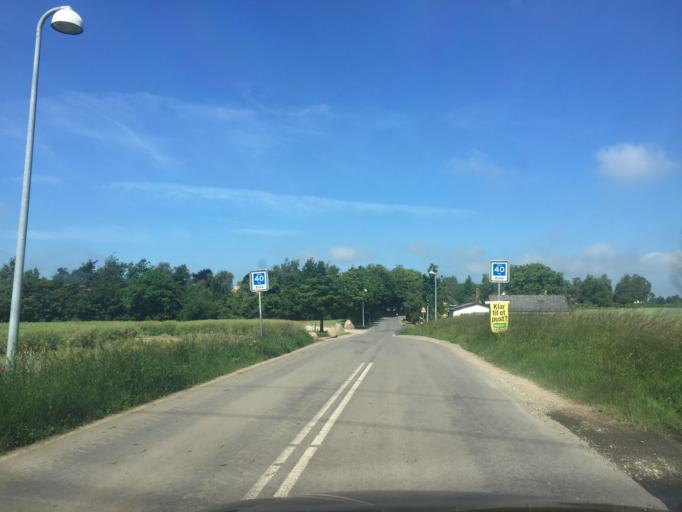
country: DK
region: Capital Region
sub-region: Hoje-Taastrup Kommune
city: Flong
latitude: 55.6746
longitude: 12.2069
